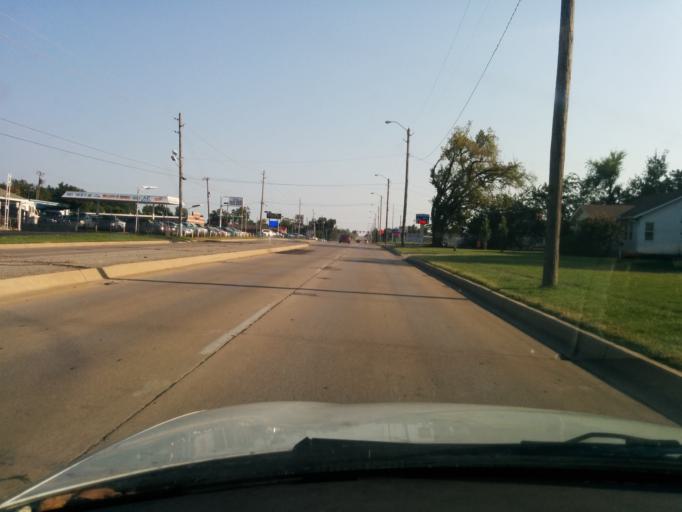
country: US
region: Oklahoma
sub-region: Tulsa County
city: Tulsa
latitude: 36.1437
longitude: -95.8868
